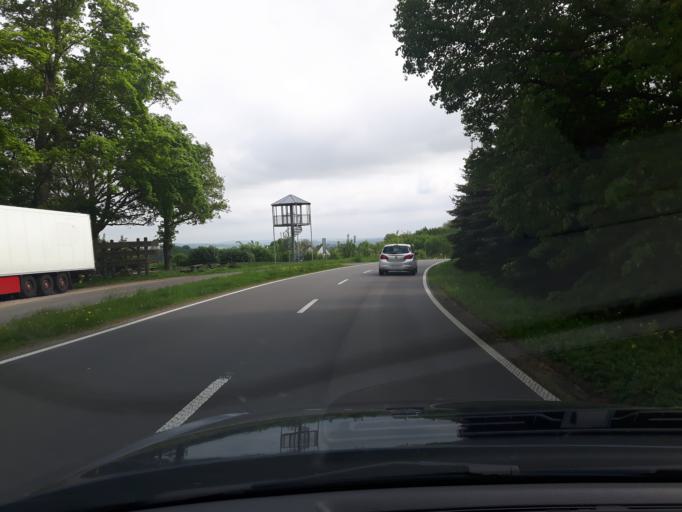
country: DE
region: Mecklenburg-Vorpommern
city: Gross Wokern
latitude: 53.6446
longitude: 12.4901
